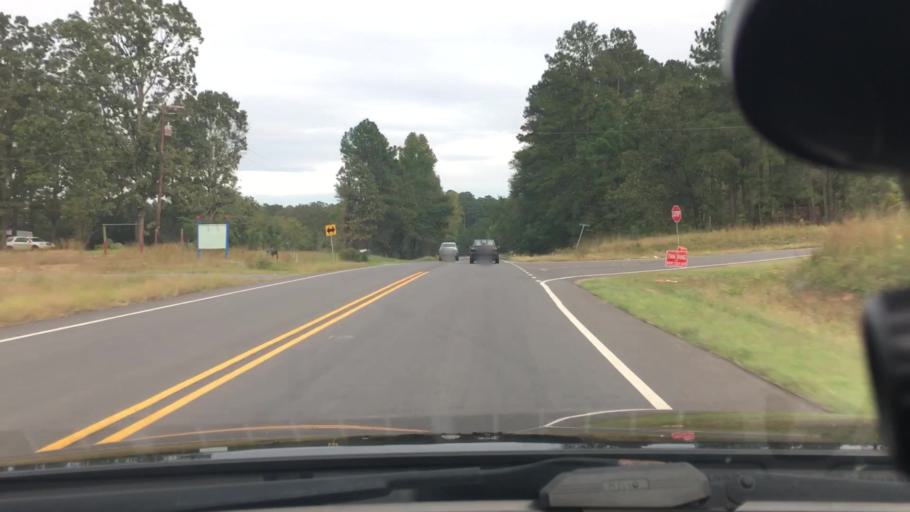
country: US
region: North Carolina
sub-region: Montgomery County
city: Biscoe
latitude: 35.3603
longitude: -79.7540
